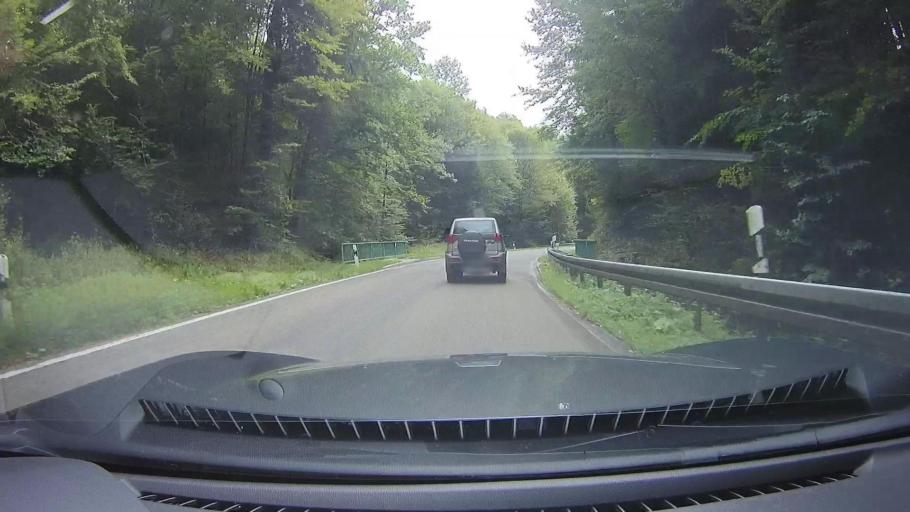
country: DE
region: Baden-Wuerttemberg
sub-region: Regierungsbezirk Stuttgart
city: Spiegelberg
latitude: 49.0470
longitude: 9.4215
